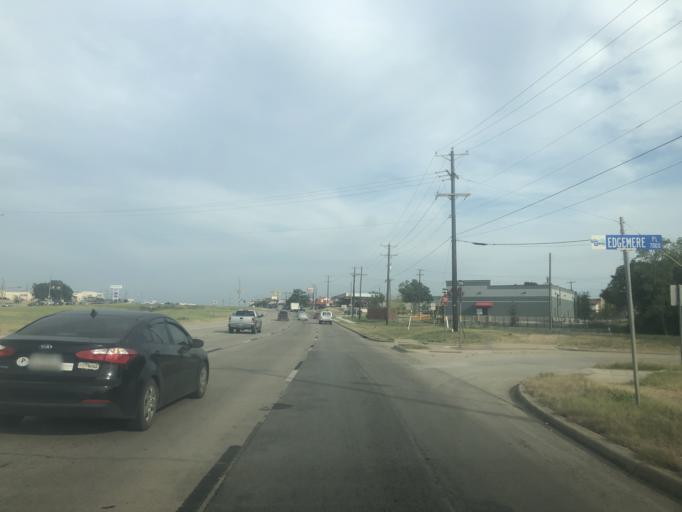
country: US
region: Texas
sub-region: Tarrant County
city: Lake Worth
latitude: 32.8166
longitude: -97.4414
